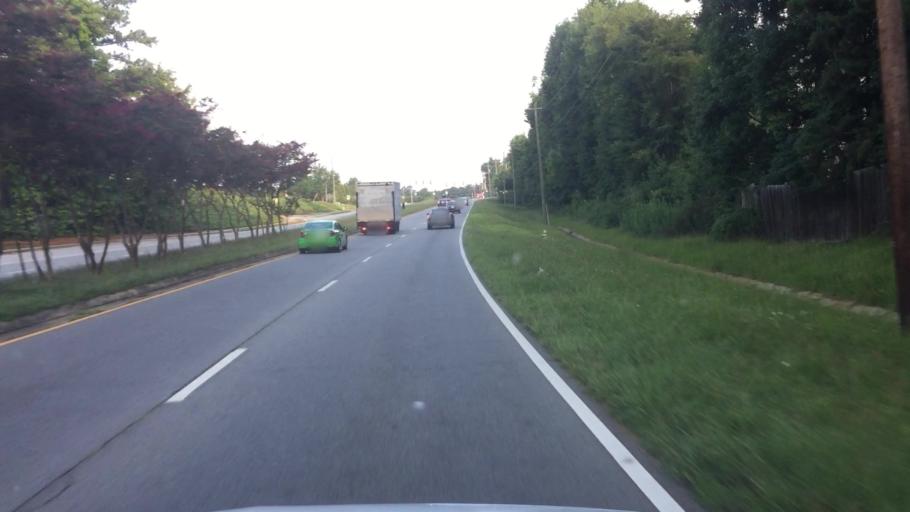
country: US
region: Georgia
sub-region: DeKalb County
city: Panthersville
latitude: 33.6798
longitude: -84.2234
